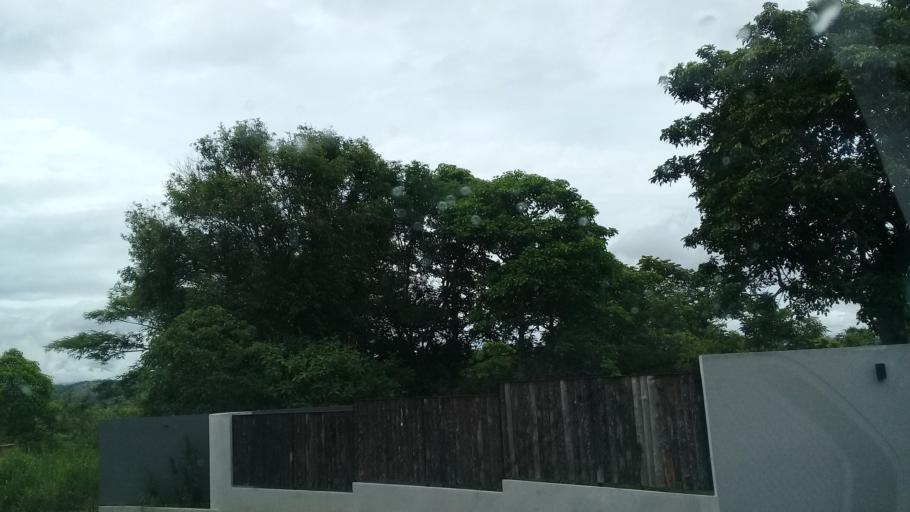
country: MX
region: Veracruz
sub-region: Emiliano Zapata
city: Jacarandas
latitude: 19.5087
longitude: -96.8439
